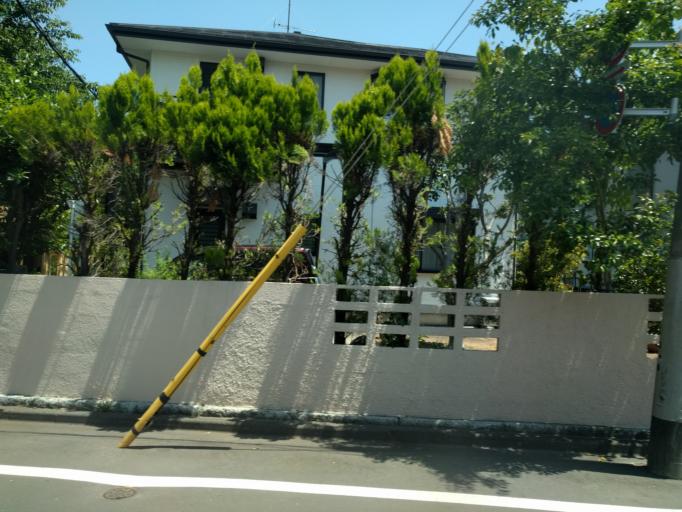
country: JP
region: Tokyo
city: Chofugaoka
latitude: 35.6469
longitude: 139.5967
